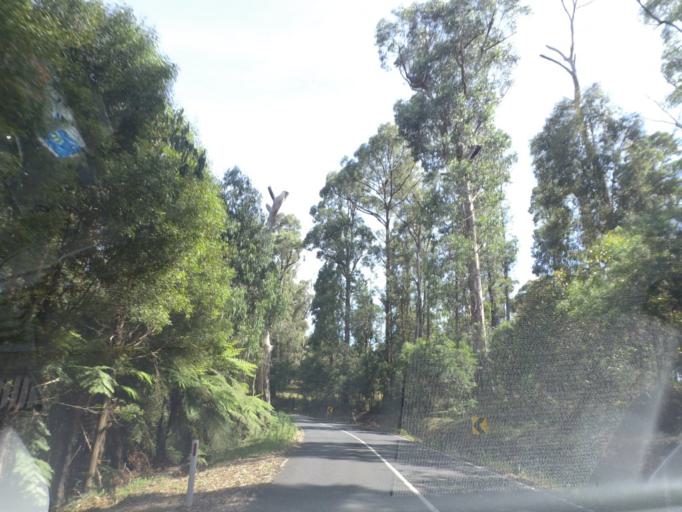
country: AU
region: Victoria
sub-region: Nillumbik
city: Saint Andrews
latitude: -37.5409
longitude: 145.3390
